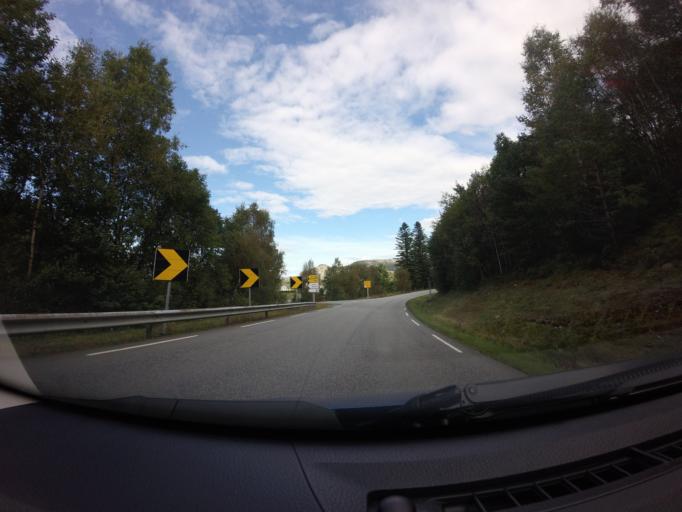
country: NO
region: Rogaland
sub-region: Forsand
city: Forsand
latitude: 58.8904
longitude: 6.0095
